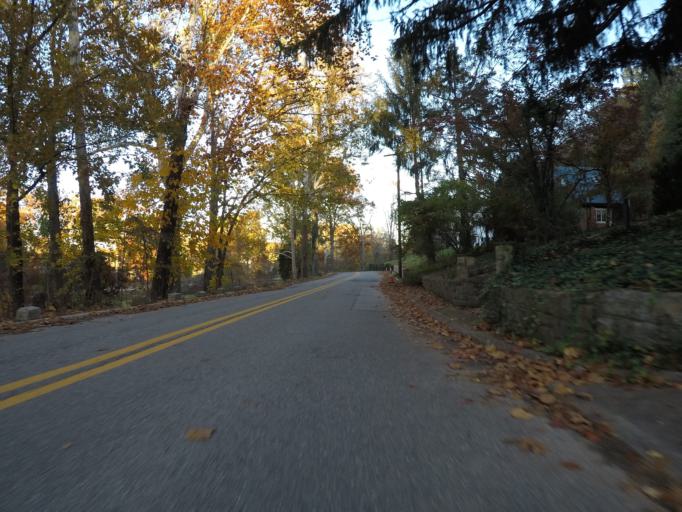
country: US
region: West Virginia
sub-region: Cabell County
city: Huntington
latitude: 38.4059
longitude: -82.4554
